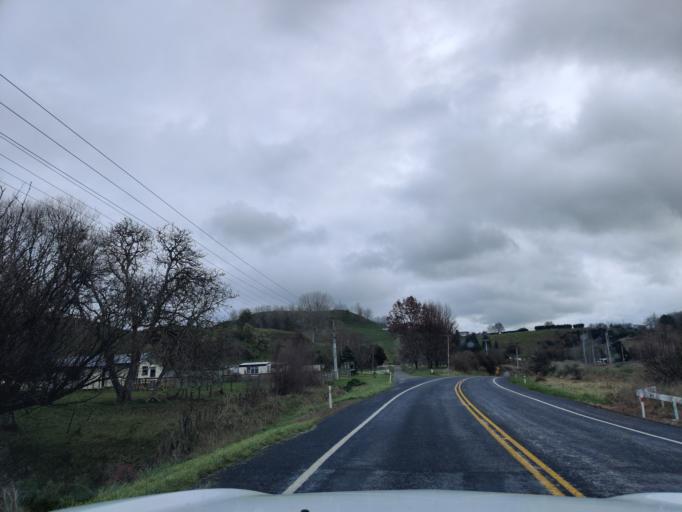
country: NZ
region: Manawatu-Wanganui
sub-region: Ruapehu District
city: Waiouru
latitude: -39.6910
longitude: 175.8105
